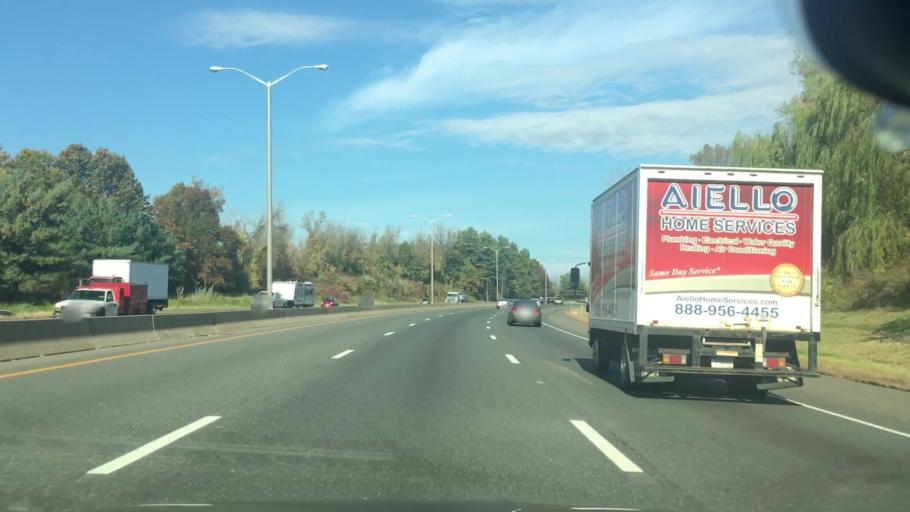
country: US
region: Connecticut
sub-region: Hartford County
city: Enfield
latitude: 41.9499
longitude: -72.6044
